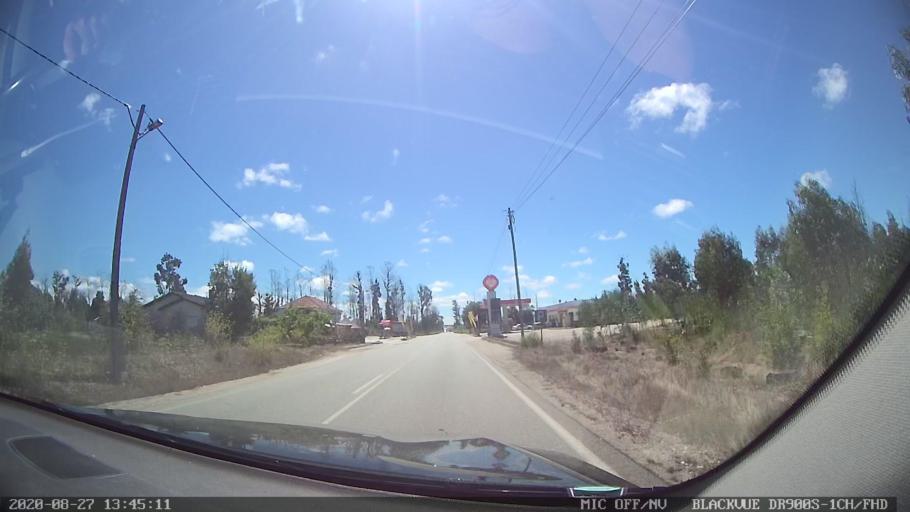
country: PT
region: Coimbra
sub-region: Mira
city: Mira
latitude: 40.4071
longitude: -8.7348
